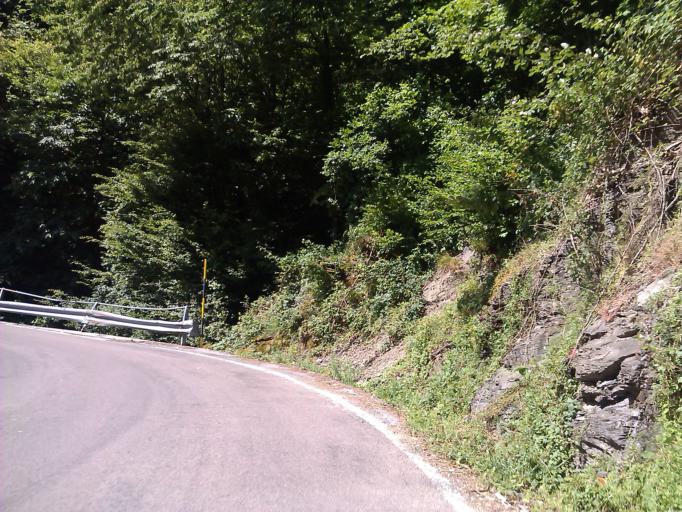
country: IT
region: Tuscany
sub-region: Provincia di Pistoia
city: Sambuca Pistoiese
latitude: 44.0995
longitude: 11.0434
